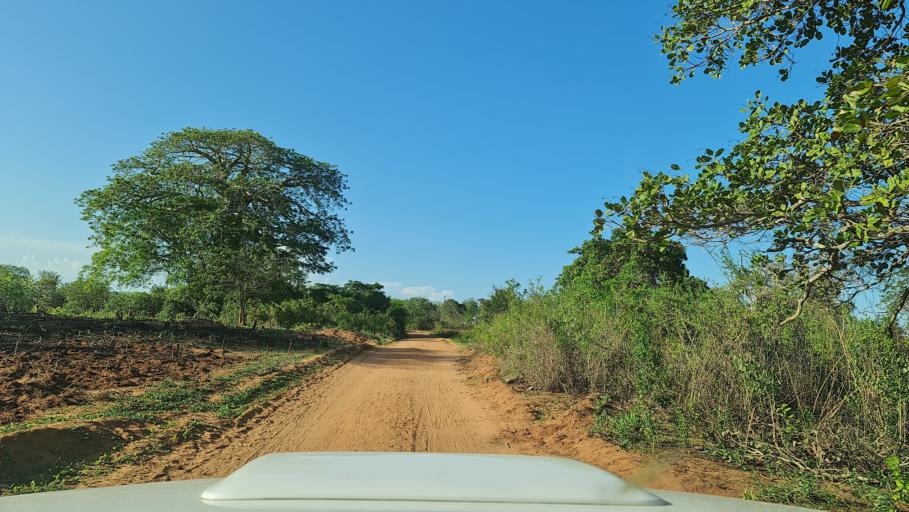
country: MZ
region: Nampula
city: Nacala
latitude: -14.7093
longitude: 40.3342
